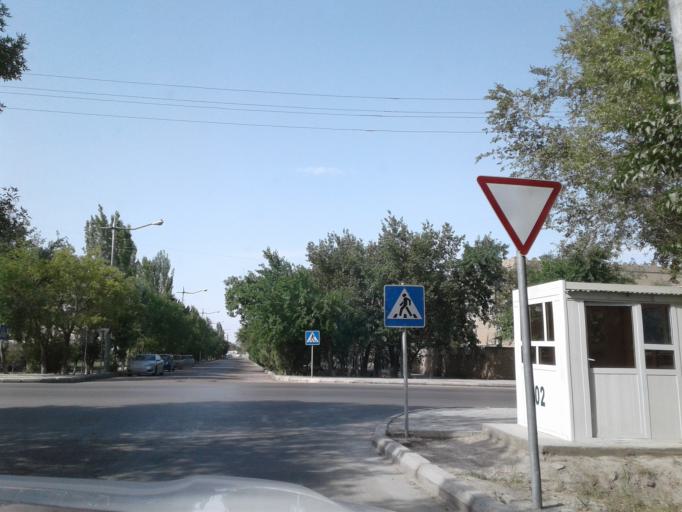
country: TM
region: Dasoguz
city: Dasoguz
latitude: 41.8370
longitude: 59.9637
